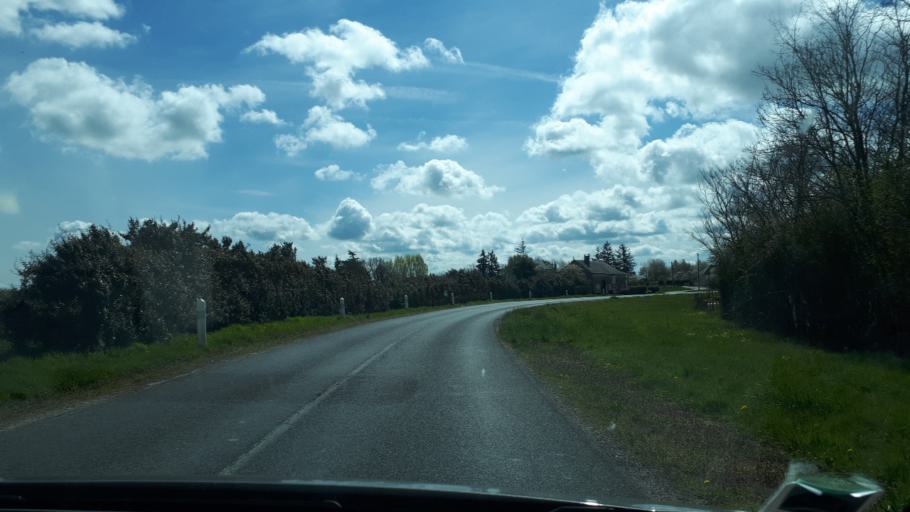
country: FR
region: Centre
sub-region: Departement du Loir-et-Cher
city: Lunay
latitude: 47.8525
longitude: 0.8927
